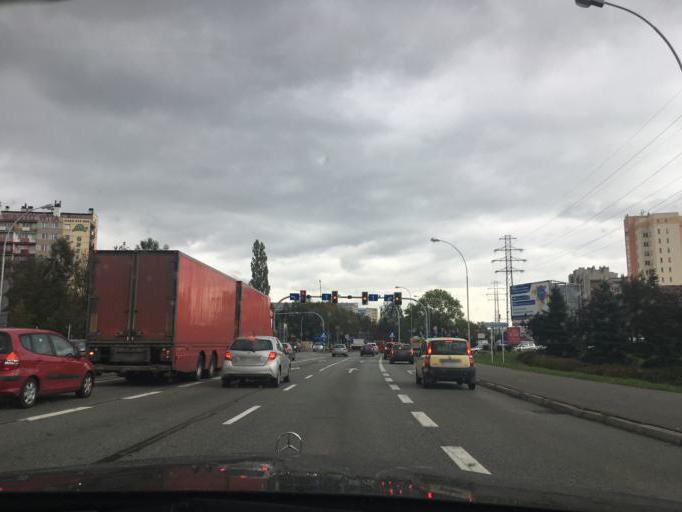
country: PL
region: Subcarpathian Voivodeship
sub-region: Rzeszow
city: Rzeszow
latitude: 50.0199
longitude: 22.0027
